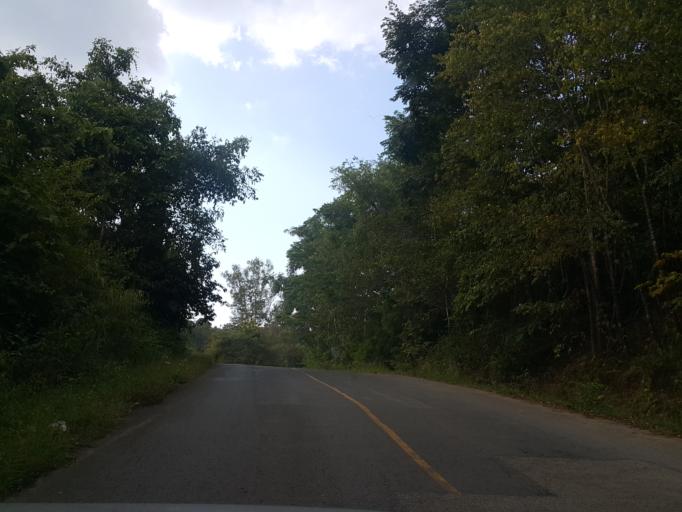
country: TH
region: Chiang Mai
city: Mae Chaem
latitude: 18.5551
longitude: 98.3920
